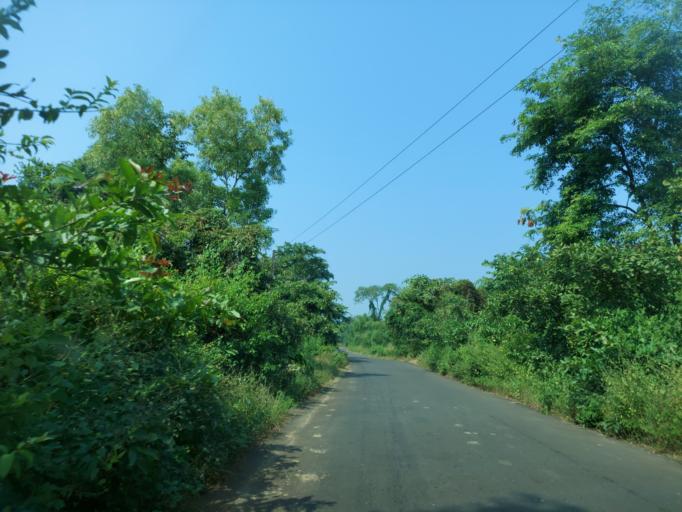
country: IN
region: Maharashtra
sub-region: Sindhudurg
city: Kudal
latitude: 15.9762
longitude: 73.6191
